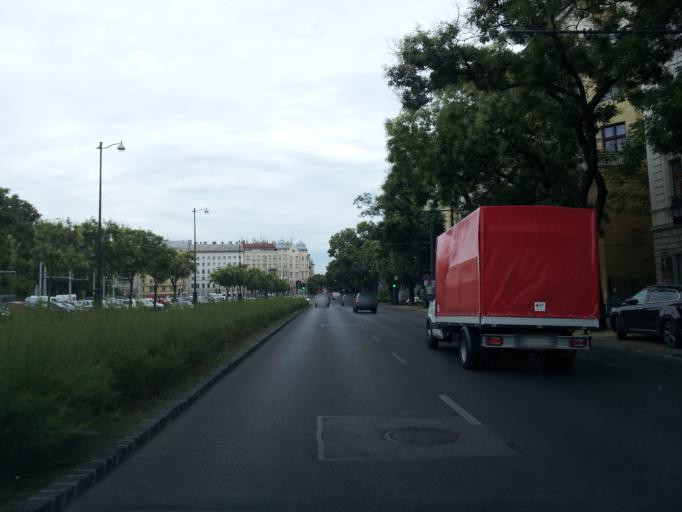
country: HU
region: Budapest
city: Budapest VII. keruelet
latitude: 47.5088
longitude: 19.0834
